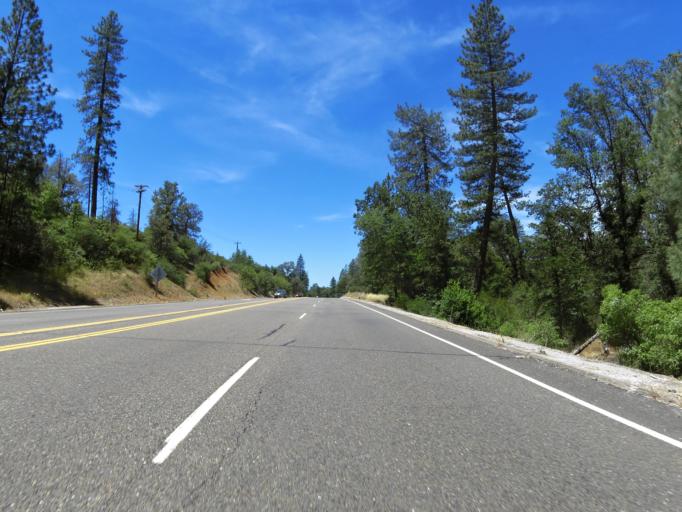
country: US
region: California
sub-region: Mariposa County
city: Midpines
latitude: 37.5222
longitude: -119.9294
